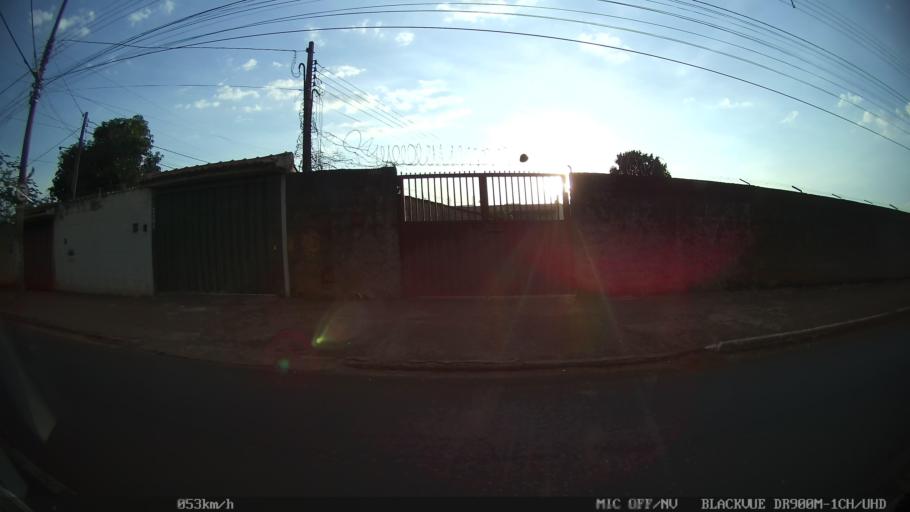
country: BR
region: Sao Paulo
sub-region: Ribeirao Preto
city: Ribeirao Preto
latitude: -21.1506
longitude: -47.8091
